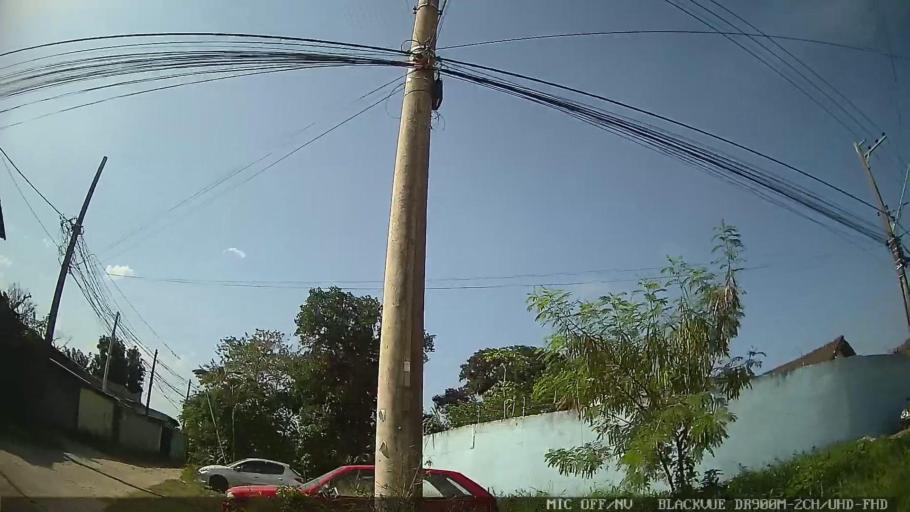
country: BR
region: Sao Paulo
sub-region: Guaruja
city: Guaruja
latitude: -23.9752
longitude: -46.1999
